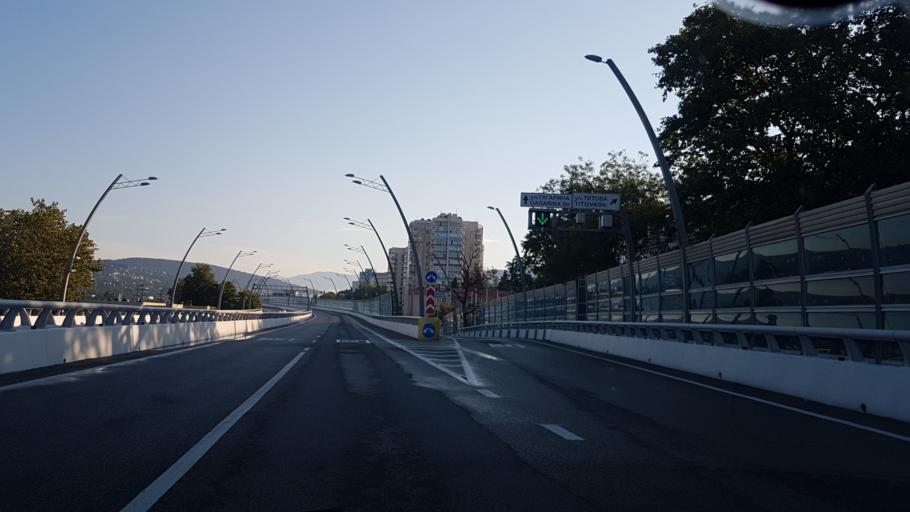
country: RU
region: Krasnodarskiy
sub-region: Sochi City
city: Sochi
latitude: 43.5932
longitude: 39.7309
